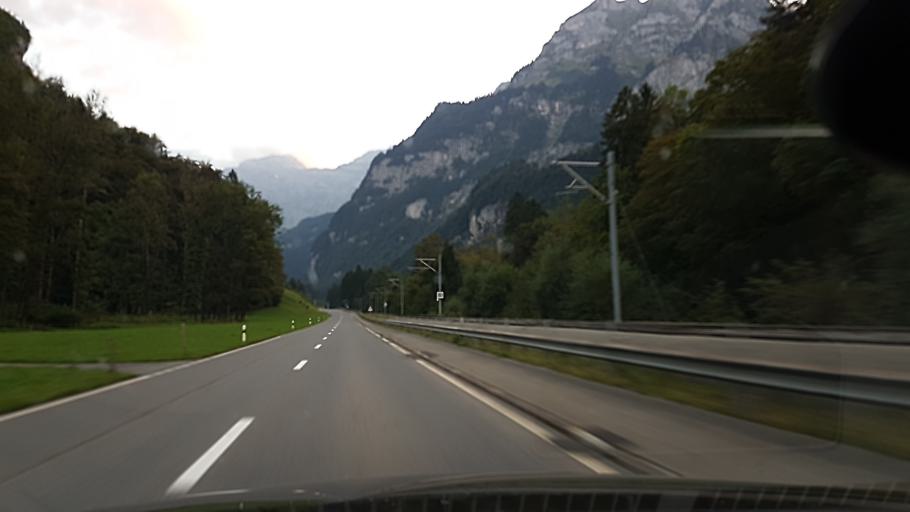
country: CH
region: Nidwalden
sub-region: Nidwalden
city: Wolfenschiessen
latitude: 46.8626
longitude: 8.3716
